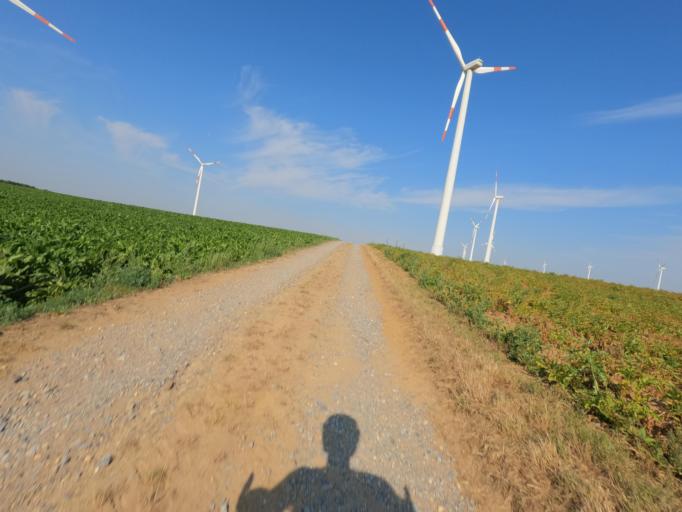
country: DE
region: North Rhine-Westphalia
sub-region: Regierungsbezirk Koln
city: Aldenhoven
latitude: 50.9256
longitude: 6.2833
